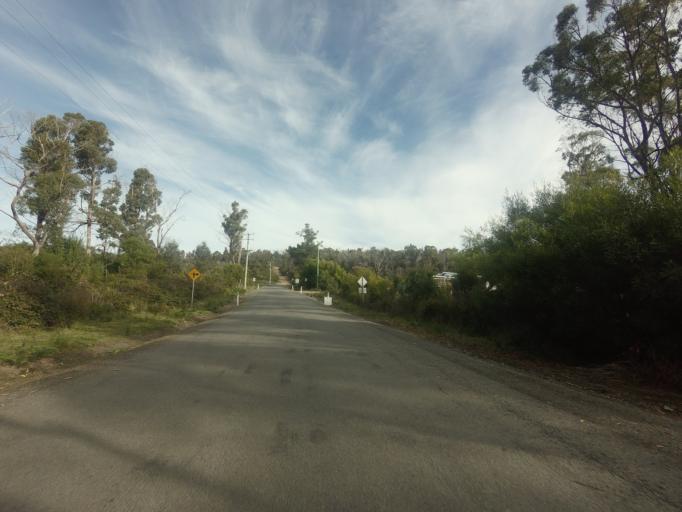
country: AU
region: Tasmania
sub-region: Sorell
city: Sorell
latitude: -42.9584
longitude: 147.8532
